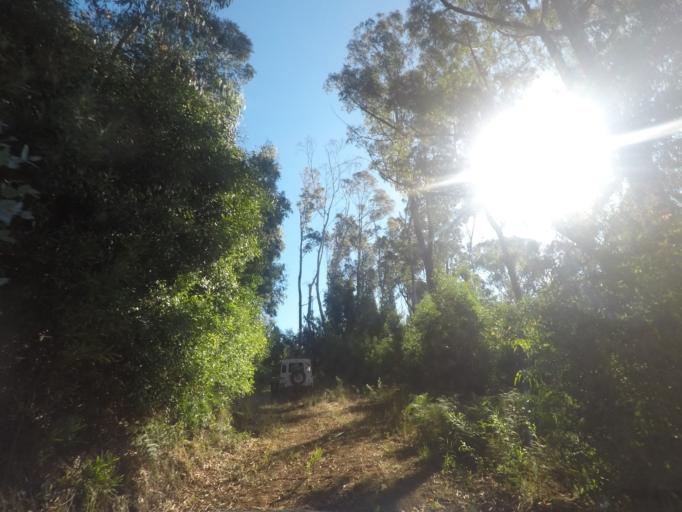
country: PT
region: Madeira
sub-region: Funchal
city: Nossa Senhora do Monte
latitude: 32.6906
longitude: -16.9133
